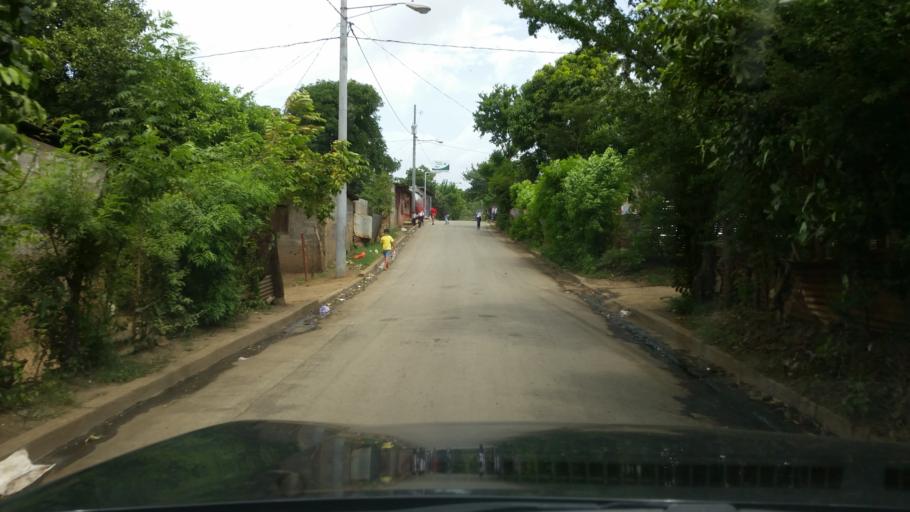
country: NI
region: Managua
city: Managua
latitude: 12.1099
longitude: -86.2166
